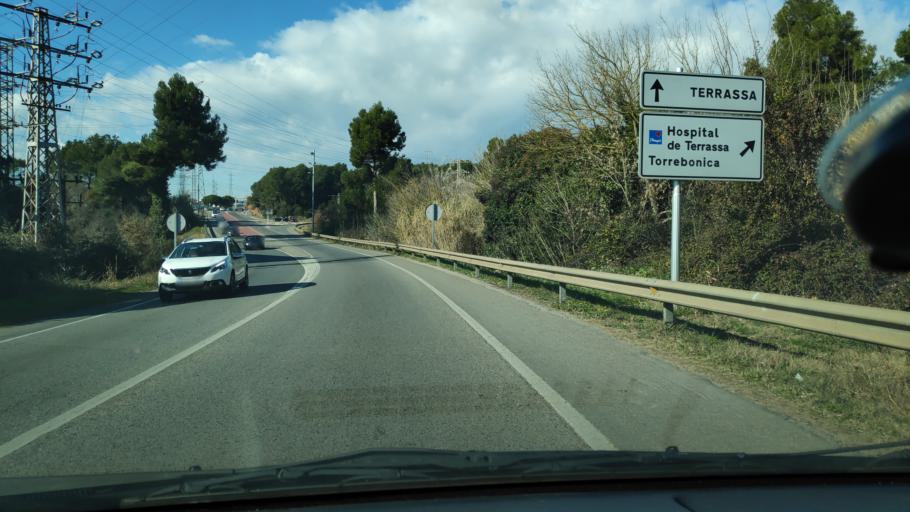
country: ES
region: Catalonia
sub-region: Provincia de Barcelona
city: Sant Quirze del Valles
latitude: 41.5538
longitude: 2.0567
